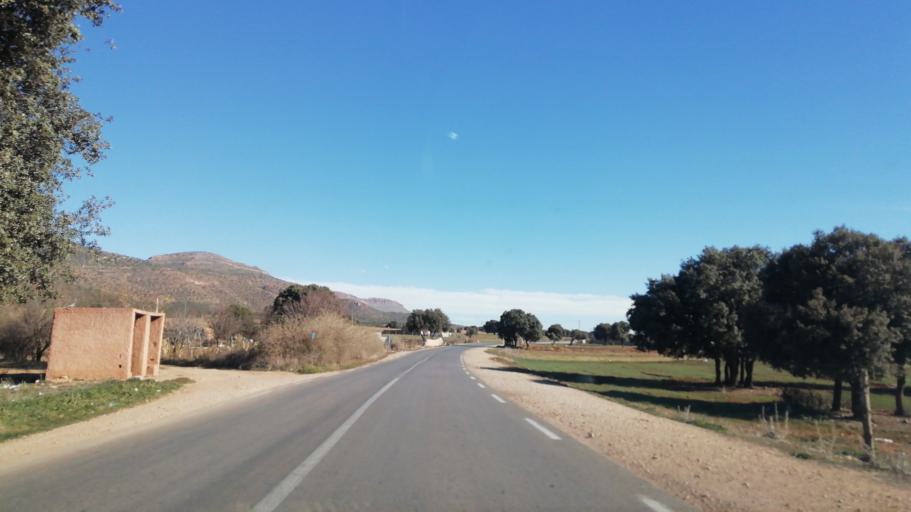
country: DZ
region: Tlemcen
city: Sebdou
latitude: 34.6954
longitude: -1.2365
